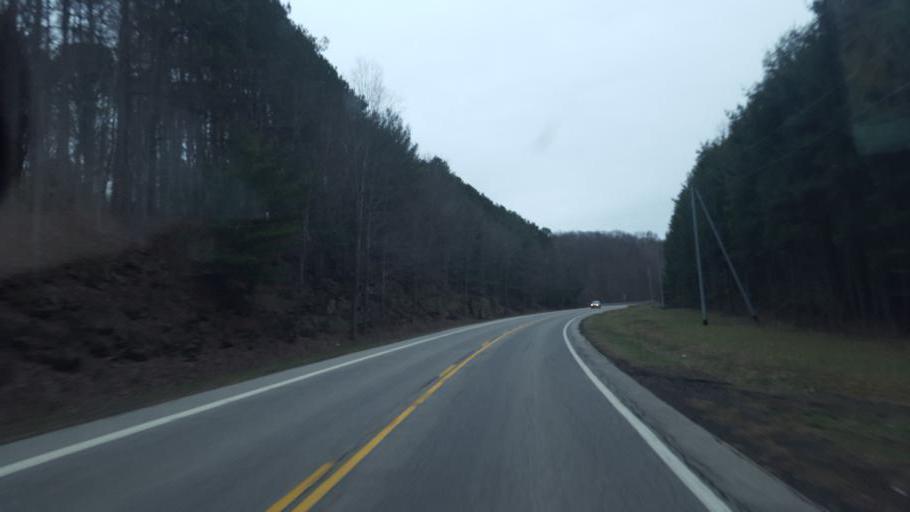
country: US
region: Ohio
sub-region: Ashland County
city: Loudonville
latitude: 40.5863
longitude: -82.2613
